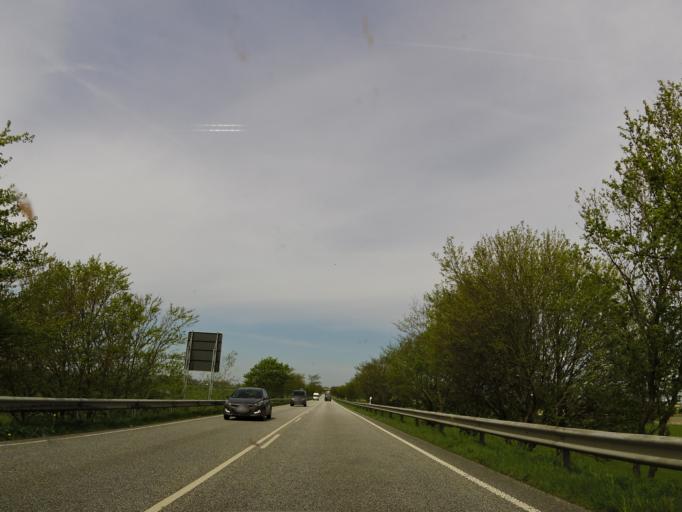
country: DE
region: Schleswig-Holstein
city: Hemme
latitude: 54.2782
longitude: 9.0045
